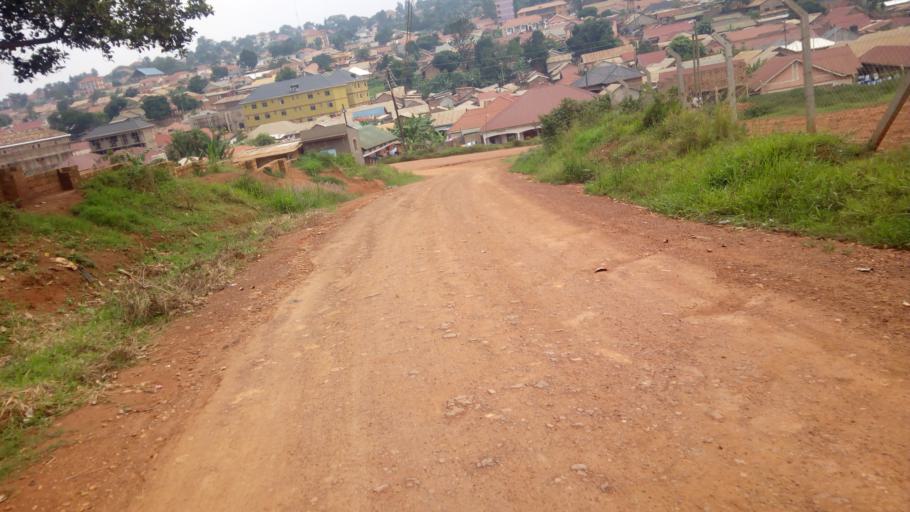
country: UG
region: Central Region
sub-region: Wakiso District
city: Kireka
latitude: 0.3173
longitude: 32.6536
